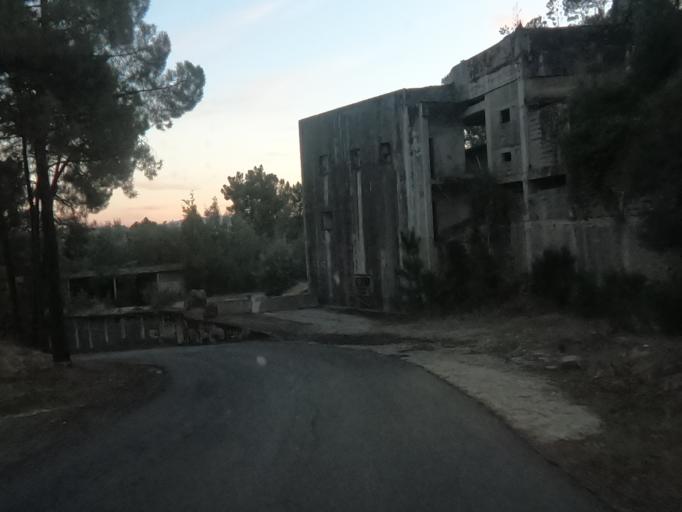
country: PT
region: Vila Real
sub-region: Vila Real
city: Vila Real
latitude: 41.2768
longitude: -7.7557
